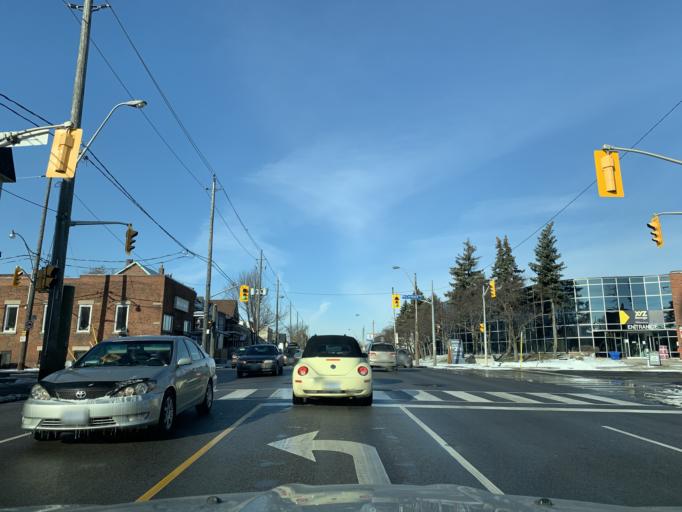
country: CA
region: Ontario
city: Toronto
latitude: 43.6771
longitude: -79.4716
